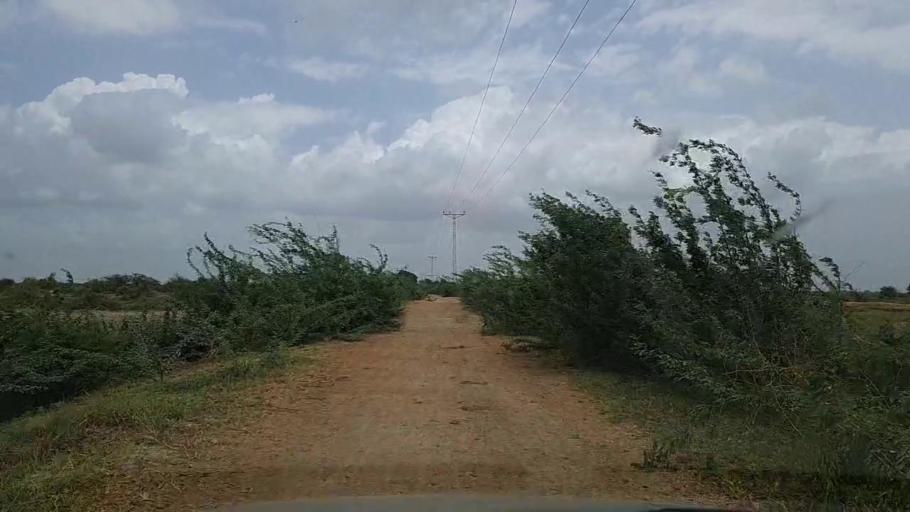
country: PK
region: Sindh
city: Thatta
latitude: 24.6109
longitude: 68.0316
